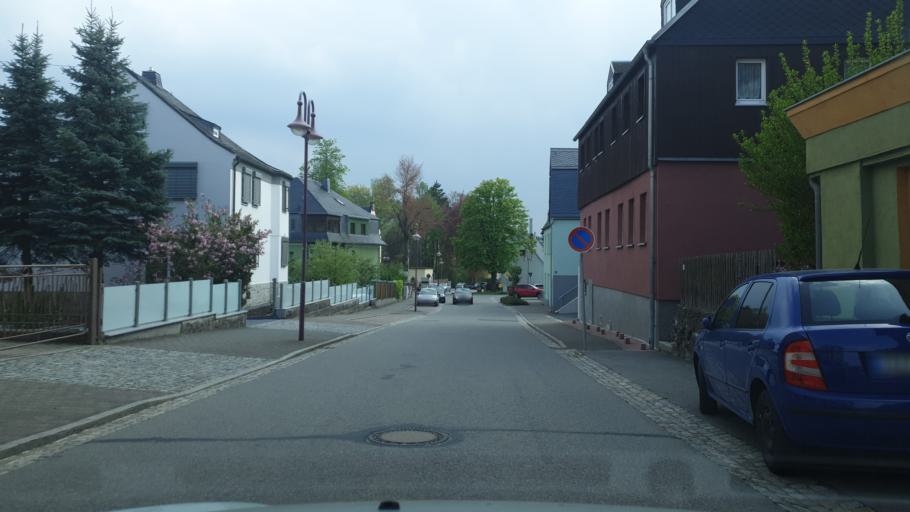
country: DE
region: Saxony
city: Lossnitz
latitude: 50.6185
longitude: 12.7283
